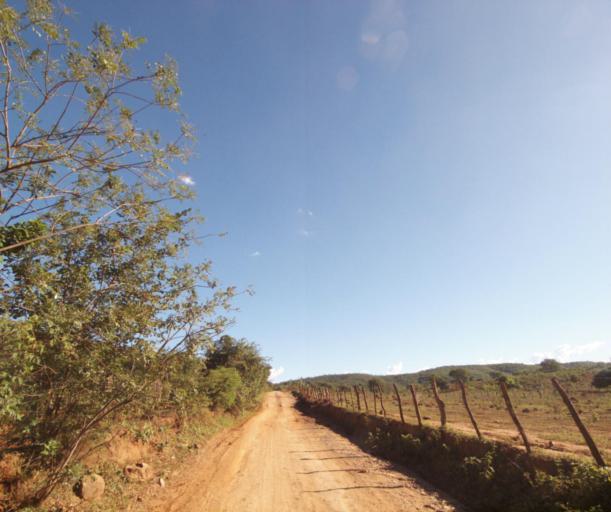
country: BR
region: Bahia
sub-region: Carinhanha
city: Carinhanha
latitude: -14.2844
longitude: -44.4691
